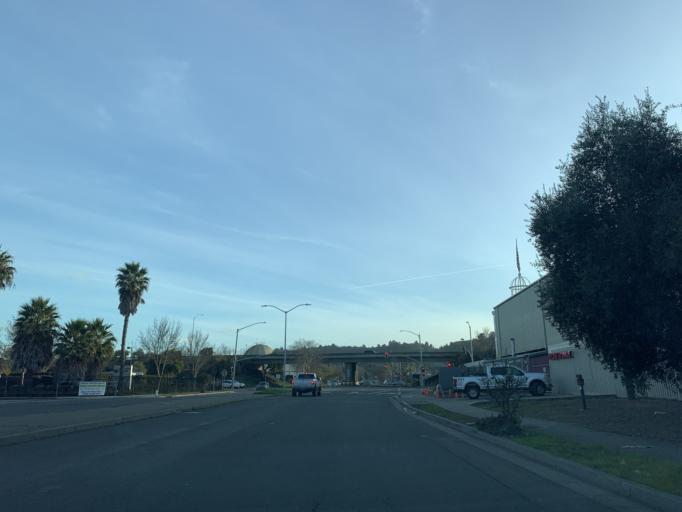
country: US
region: California
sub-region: Contra Costa County
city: Richmond
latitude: 37.9287
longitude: -122.3784
